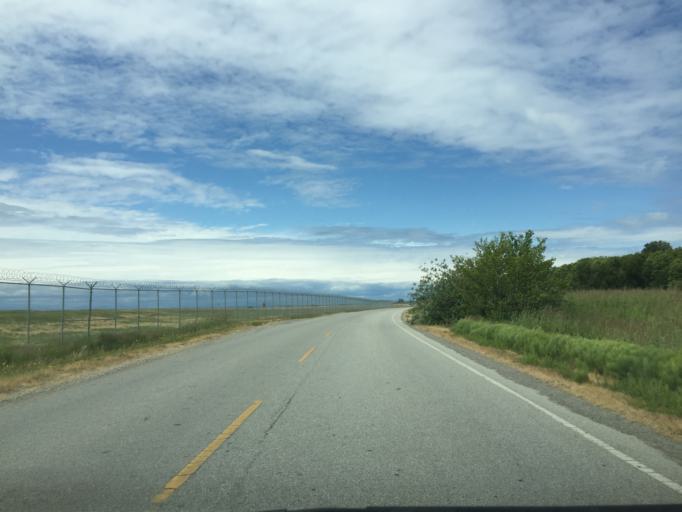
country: CA
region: British Columbia
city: Richmond
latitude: 49.2067
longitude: -123.1967
